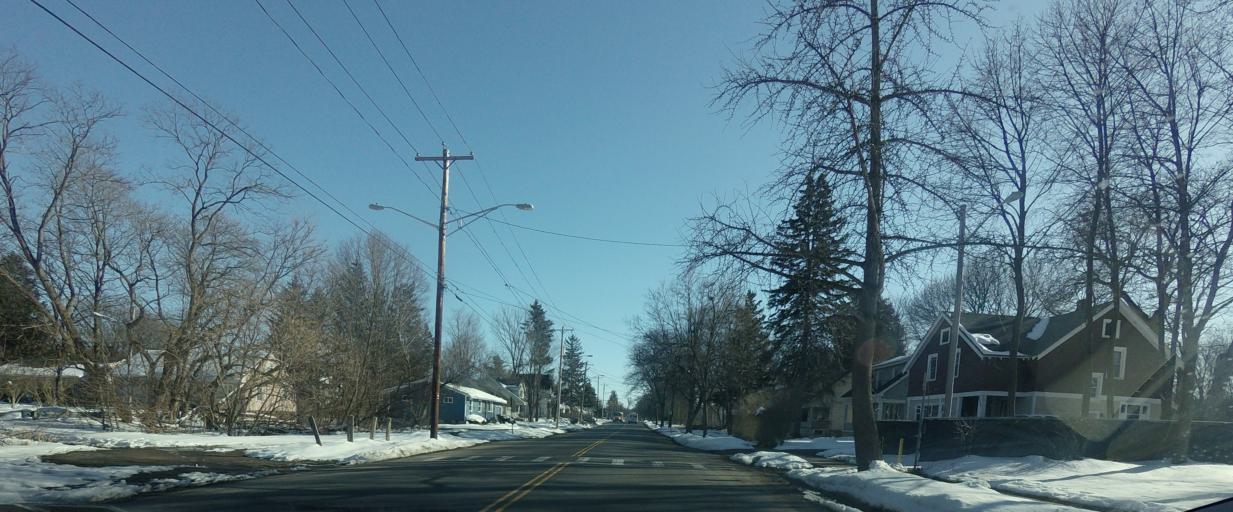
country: US
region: New York
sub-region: Onondaga County
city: Nedrow
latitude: 43.0071
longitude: -76.1474
